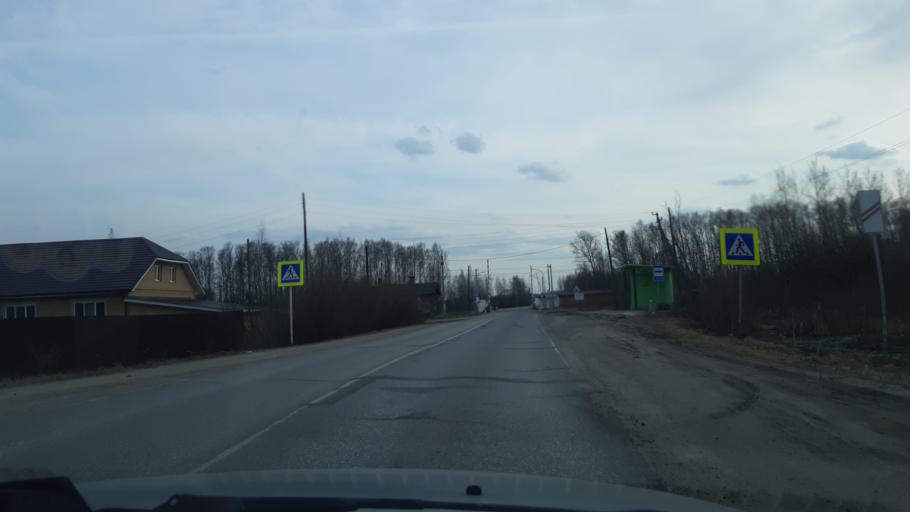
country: RU
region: Vladimir
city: Luknovo
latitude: 56.2240
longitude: 42.0349
